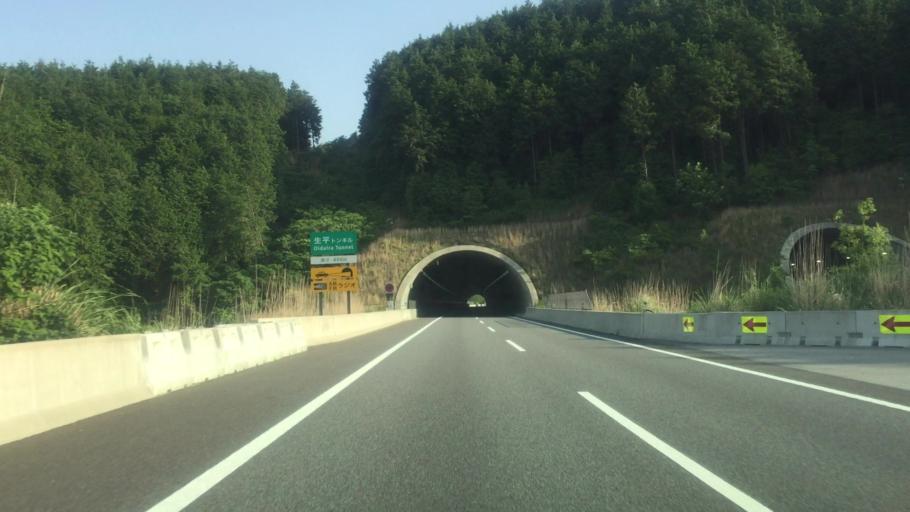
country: JP
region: Aichi
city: Okazaki
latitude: 34.9381
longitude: 137.2604
